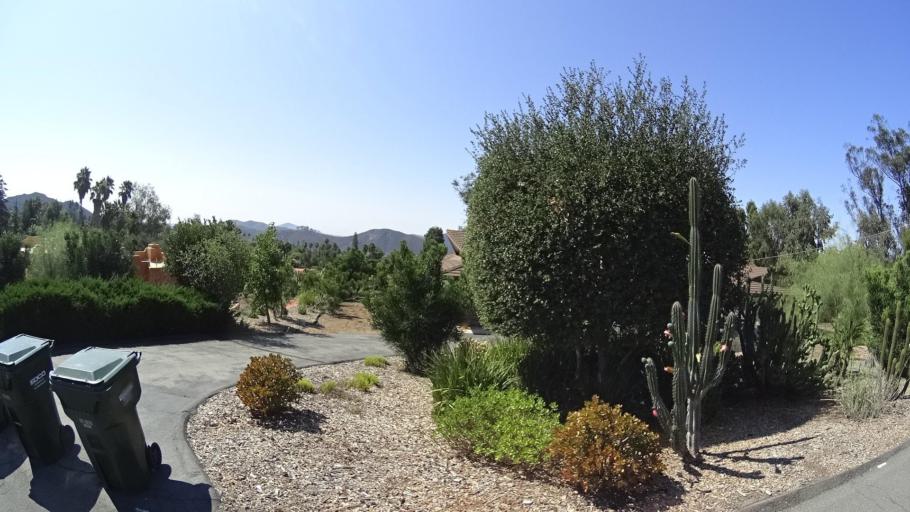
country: US
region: California
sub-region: San Diego County
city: Escondido
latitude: 33.0798
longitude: -117.0973
